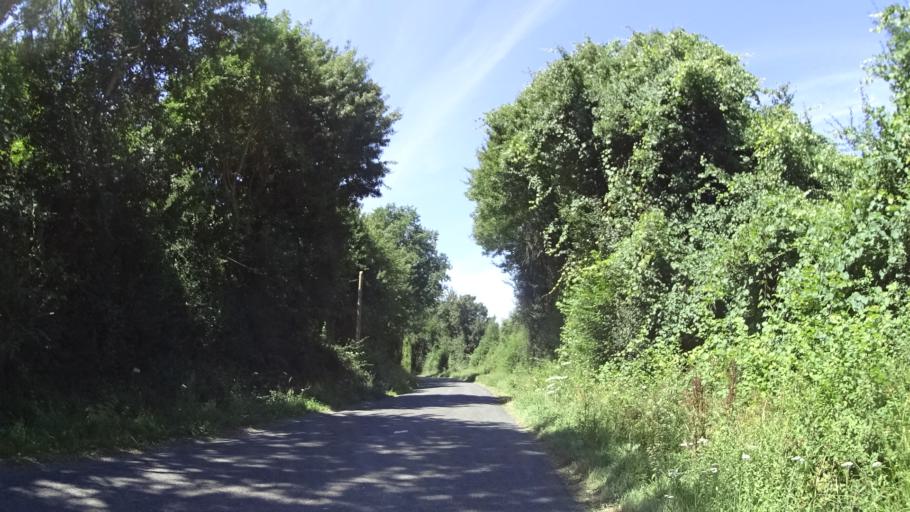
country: FR
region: Pays de la Loire
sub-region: Departement de Maine-et-Loire
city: La Poueze
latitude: 47.6323
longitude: -0.7808
